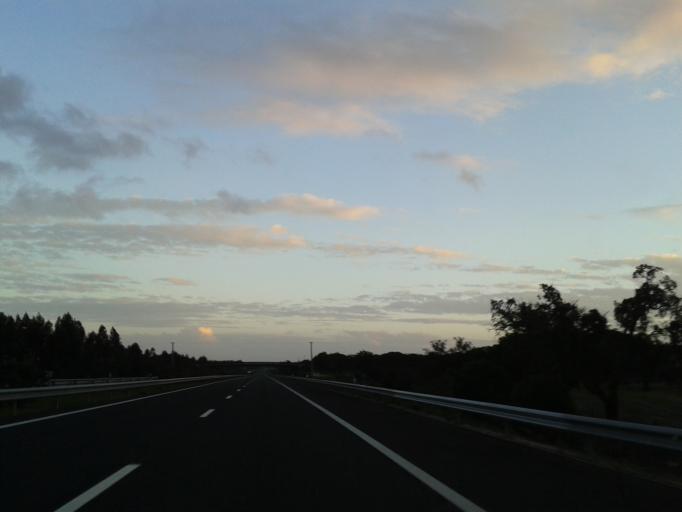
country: PT
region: Santarem
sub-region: Benavente
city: Poceirao
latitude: 38.8011
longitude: -8.6980
